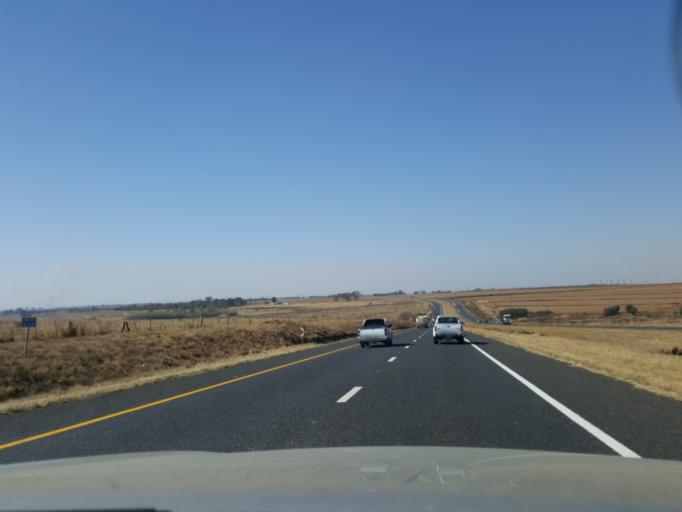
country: ZA
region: Mpumalanga
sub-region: Nkangala District Municipality
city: Delmas
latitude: -26.0682
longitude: 28.7760
